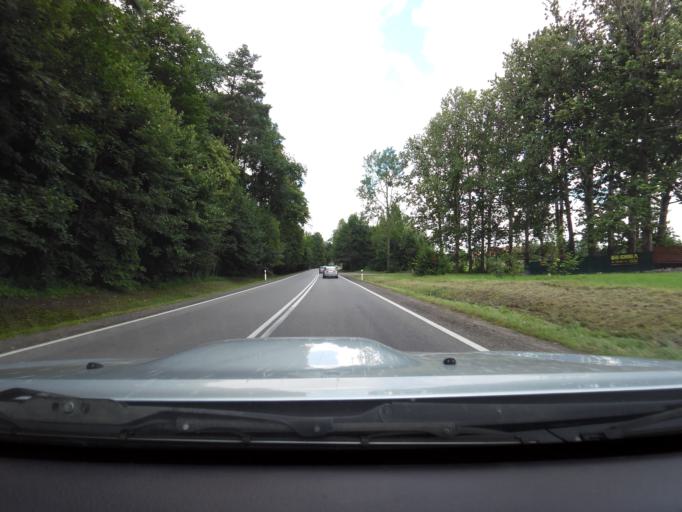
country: PL
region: Pomeranian Voivodeship
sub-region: Powiat malborski
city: Malbork
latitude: 54.0043
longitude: 19.0064
